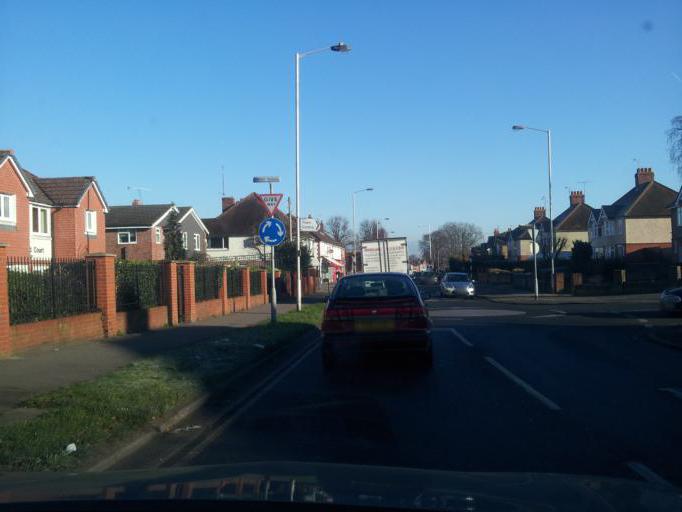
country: GB
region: England
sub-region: West Berkshire
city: Tilehurst
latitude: 51.4561
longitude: -1.0451
